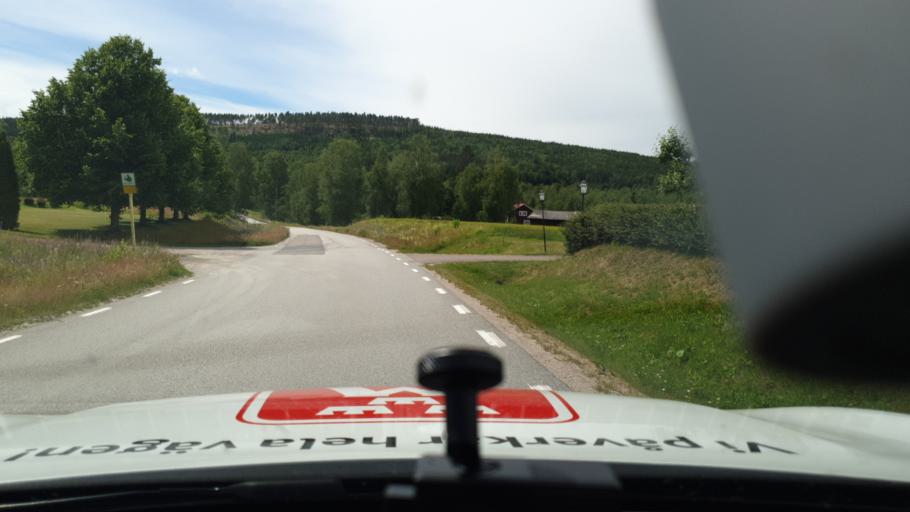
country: SE
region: Vaermland
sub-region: Hagfors Kommun
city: Ekshaerad
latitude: 60.0709
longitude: 13.4861
